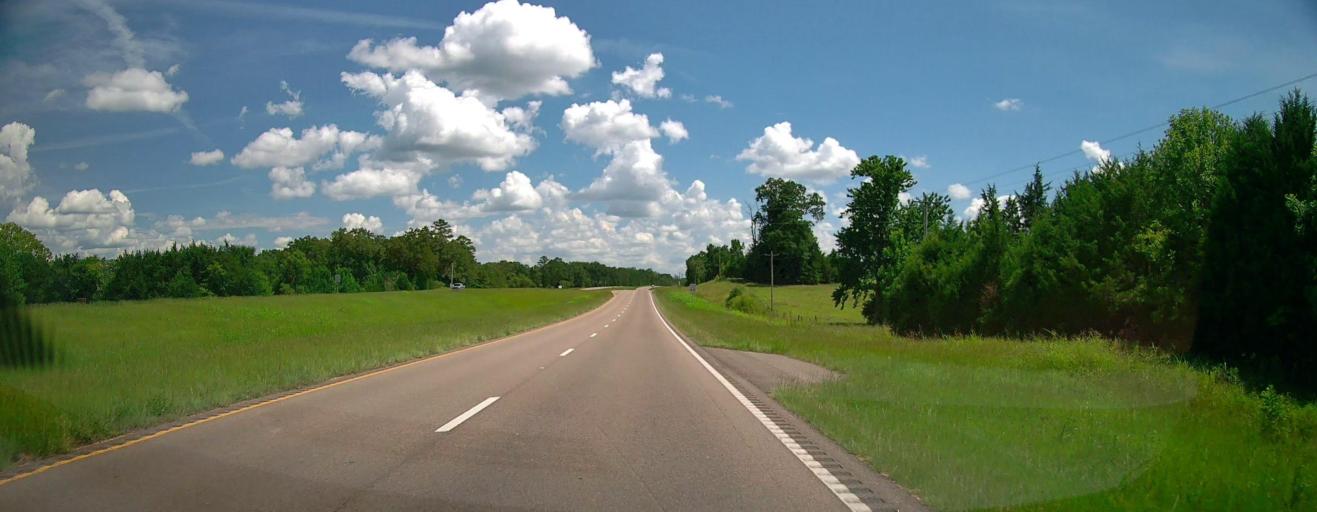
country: US
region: Mississippi
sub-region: Monroe County
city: Amory
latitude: 33.9450
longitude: -88.6006
